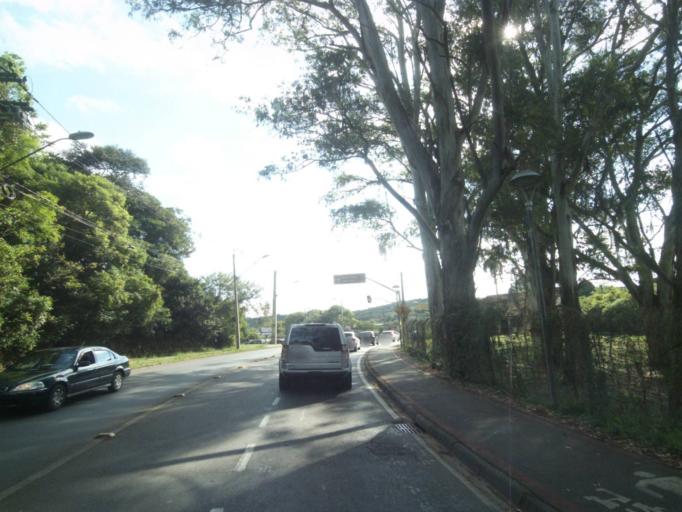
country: BR
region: Parana
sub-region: Curitiba
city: Curitiba
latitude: -25.3870
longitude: -49.3009
